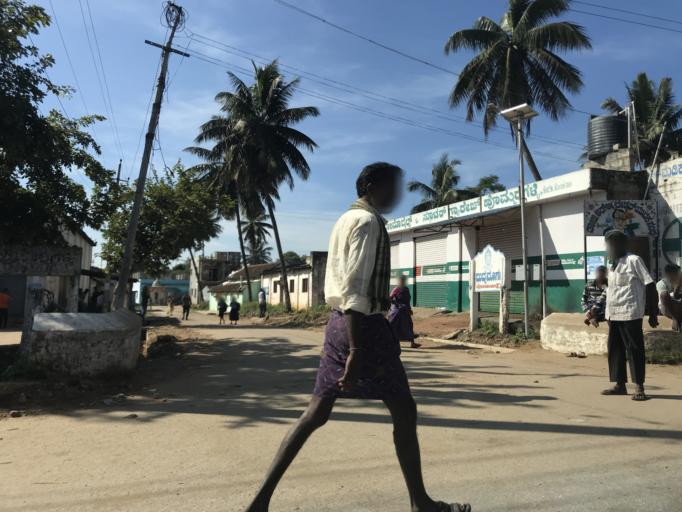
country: IN
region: Karnataka
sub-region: Mysore
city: Heggadadevankote
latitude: 12.1212
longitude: 76.4713
